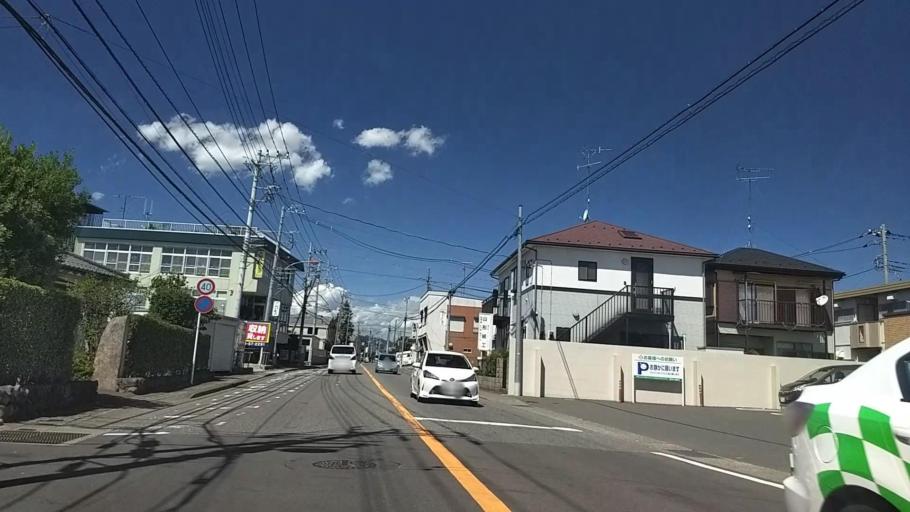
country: JP
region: Tokyo
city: Hachioji
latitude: 35.5708
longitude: 139.3205
